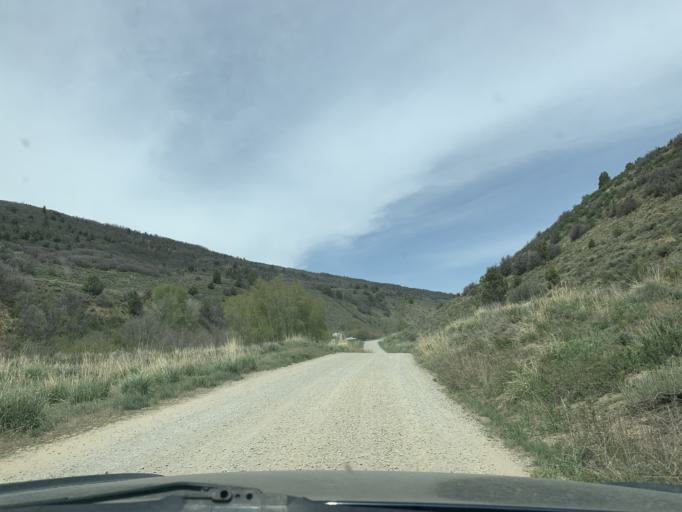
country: US
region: Utah
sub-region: Utah County
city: Mapleton
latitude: 40.1637
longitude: -111.3290
